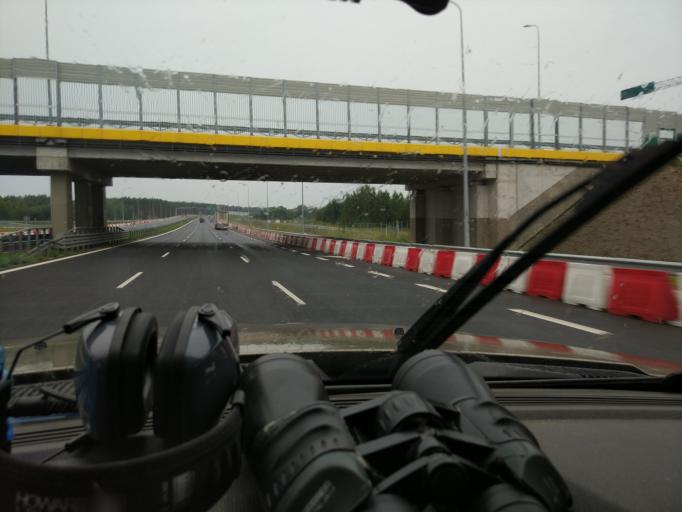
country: PL
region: Masovian Voivodeship
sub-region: Powiat wolominski
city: Kobylka
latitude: 52.3713
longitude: 21.1890
